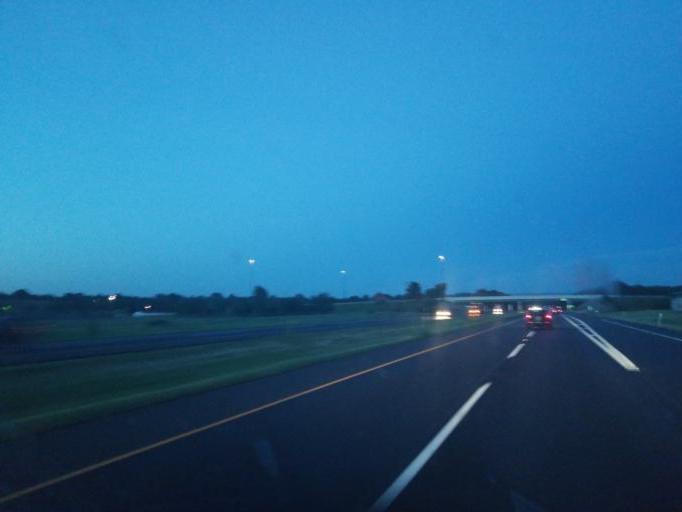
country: US
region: Indiana
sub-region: Saint Joseph County
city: Granger
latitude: 41.7311
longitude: -86.0652
